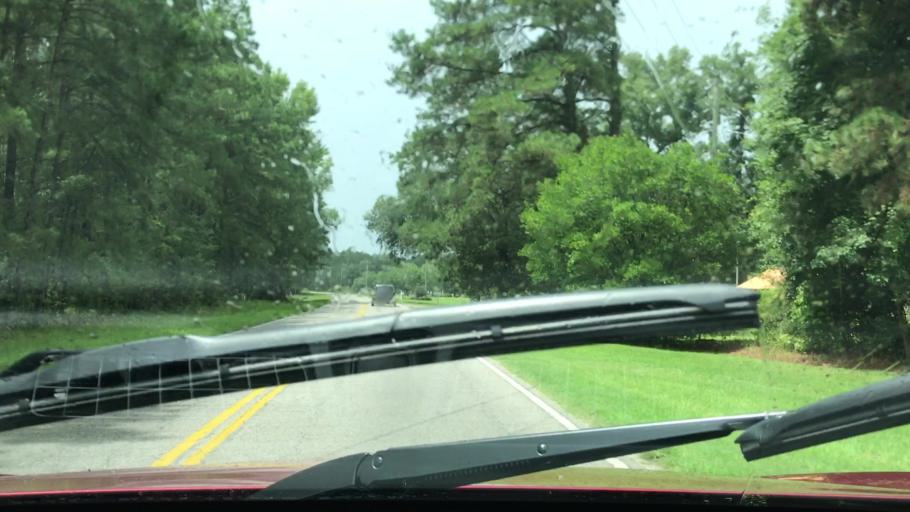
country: US
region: South Carolina
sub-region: Horry County
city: Red Hill
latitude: 33.8859
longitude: -78.9612
